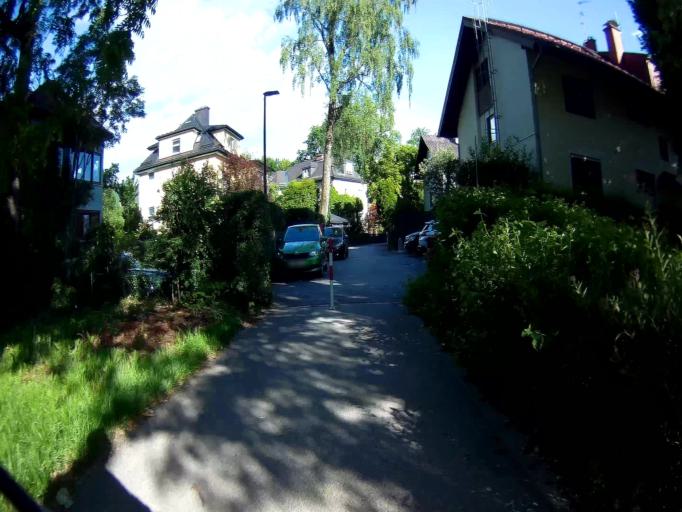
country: AT
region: Salzburg
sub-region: Salzburg Stadt
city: Salzburg
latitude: 47.7965
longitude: 13.0649
